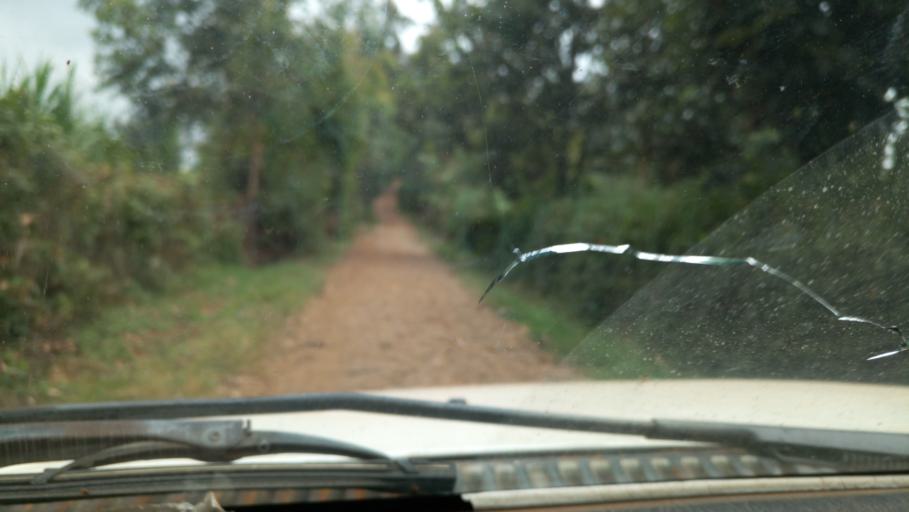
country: KE
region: Murang'a District
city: Kangema
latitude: -0.7944
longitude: 36.9205
